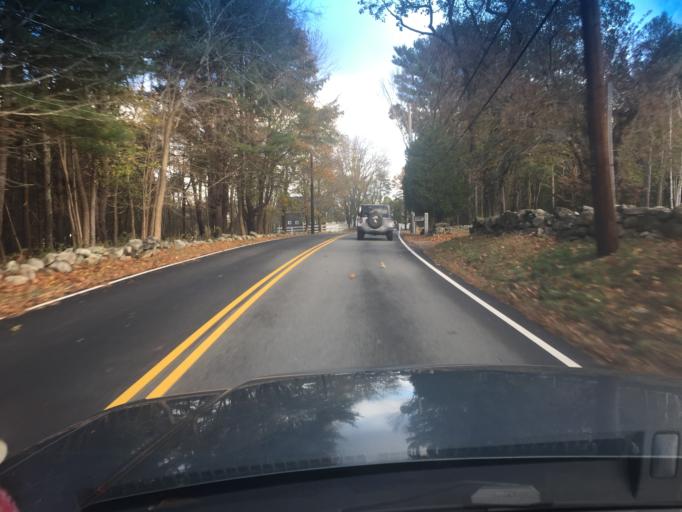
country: US
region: Massachusetts
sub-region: Norfolk County
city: Medfield
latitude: 42.2001
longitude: -71.3121
